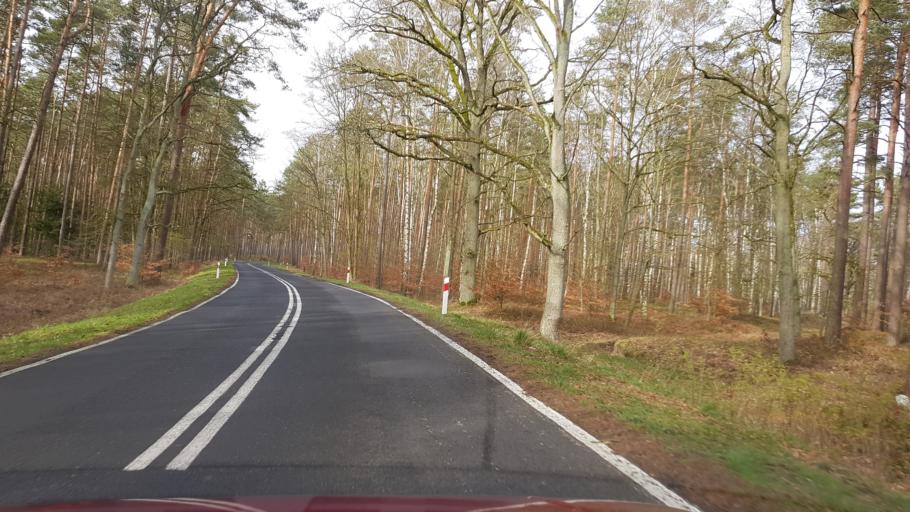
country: PL
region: West Pomeranian Voivodeship
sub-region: Powiat policki
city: Nowe Warpno
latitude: 53.6798
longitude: 14.3584
